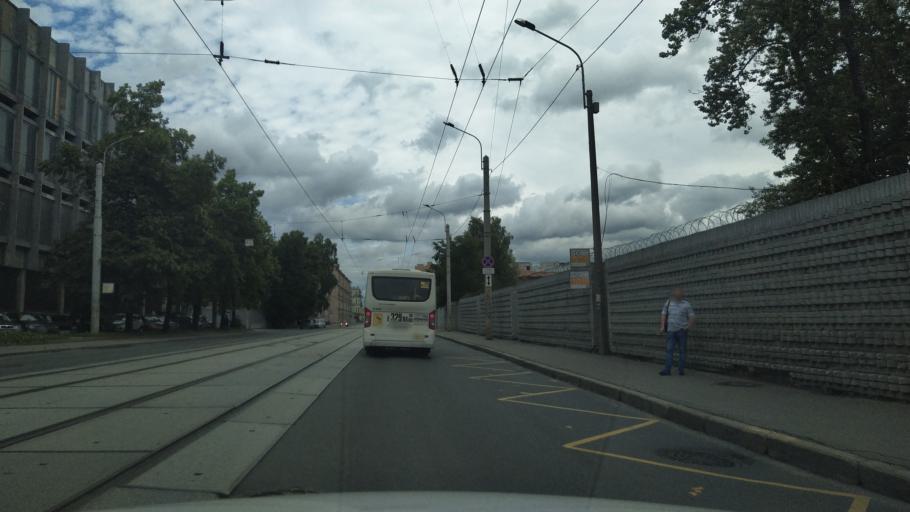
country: RU
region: Leningrad
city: Finlyandskiy
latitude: 59.9603
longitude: 30.3767
